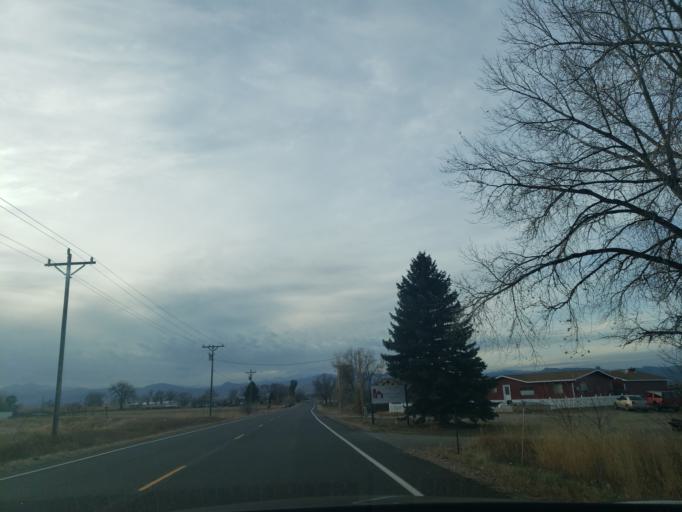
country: US
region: Colorado
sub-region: Weld County
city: Windsor
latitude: 40.4648
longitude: -104.9989
